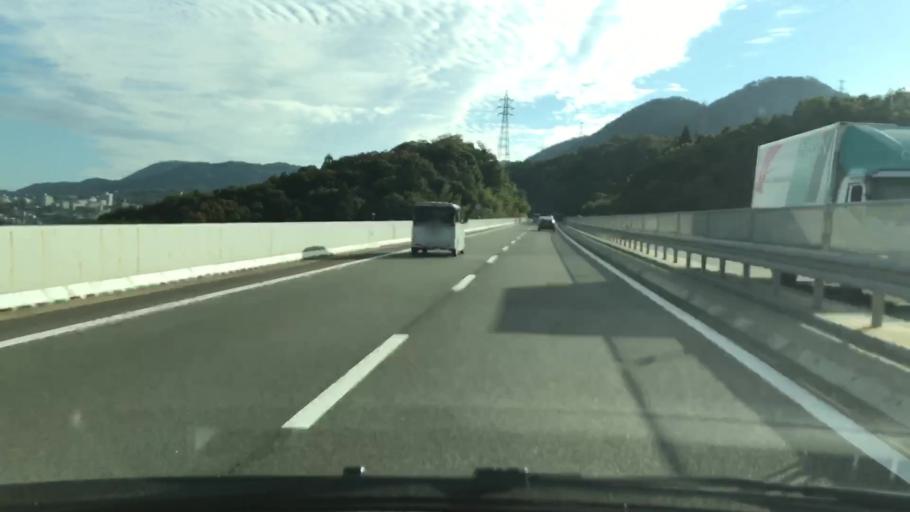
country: JP
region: Hyogo
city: Kobe
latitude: 34.7602
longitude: 135.1696
